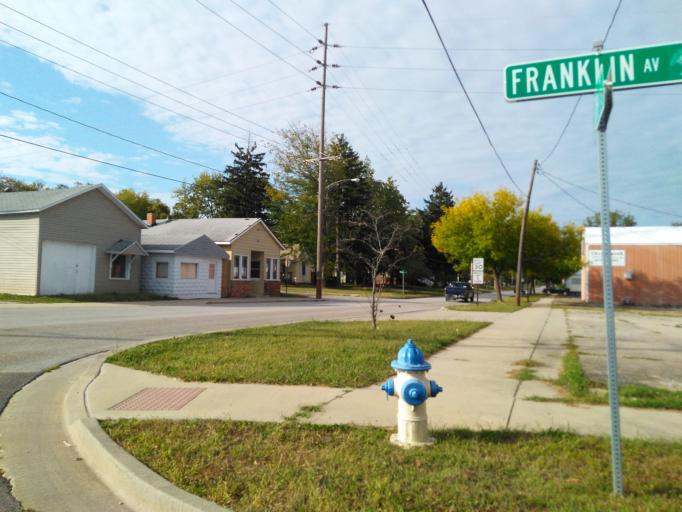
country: US
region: Illinois
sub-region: Bond County
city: Greenville
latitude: 38.8846
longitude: -89.4143
